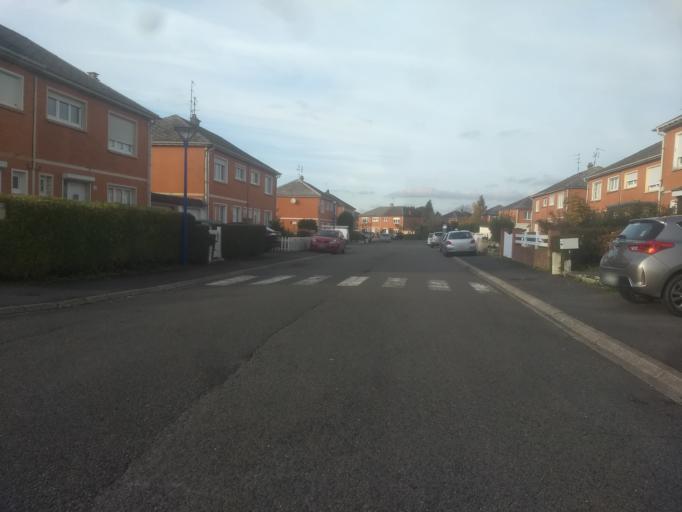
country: FR
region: Nord-Pas-de-Calais
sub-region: Departement du Pas-de-Calais
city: Beaurains
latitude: 50.2641
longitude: 2.7775
